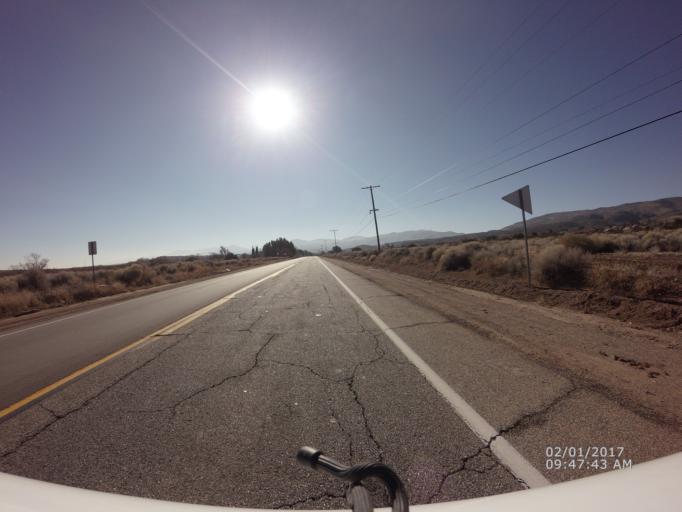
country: US
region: California
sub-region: Los Angeles County
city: Palmdale
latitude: 34.5476
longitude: -118.1109
